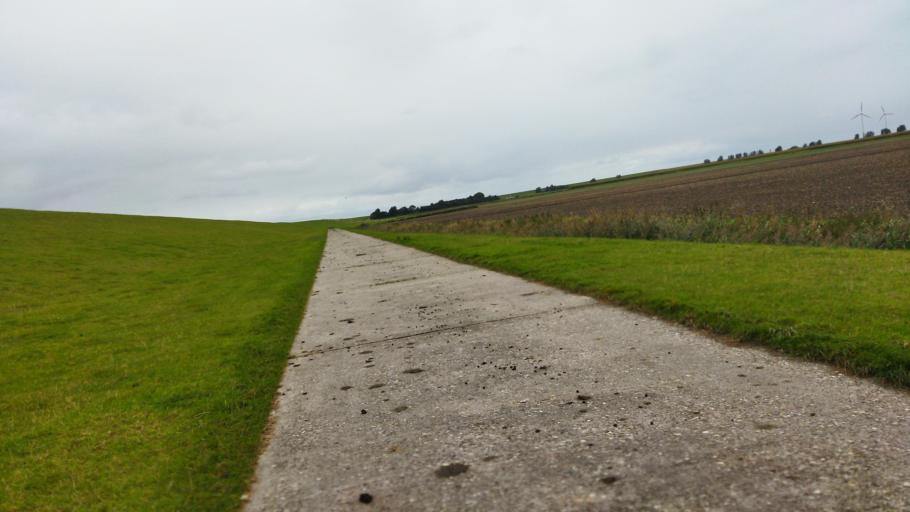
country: DE
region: Lower Saxony
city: Hinte
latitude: 53.4751
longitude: 7.0321
